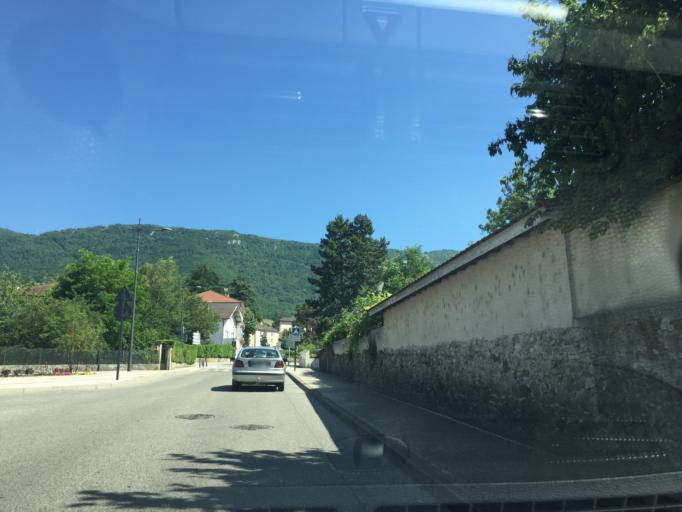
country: FR
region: Rhone-Alpes
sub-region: Departement de la Drome
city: Saint-Jean-en-Royans
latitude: 45.0213
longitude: 5.2907
